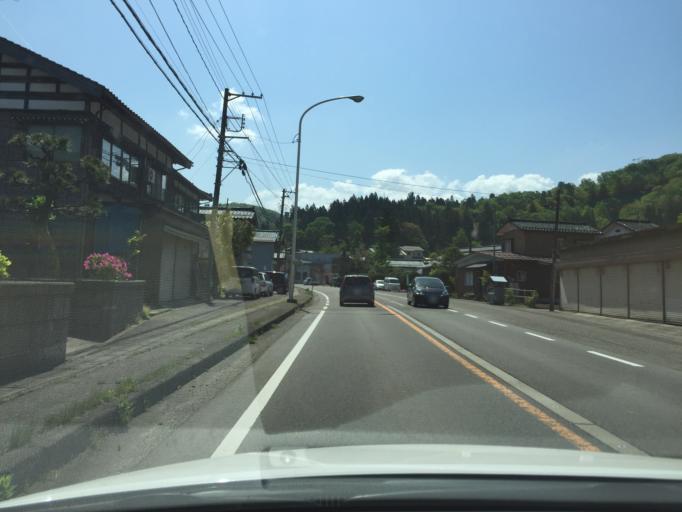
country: JP
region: Niigata
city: Kamo
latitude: 37.6274
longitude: 139.0990
